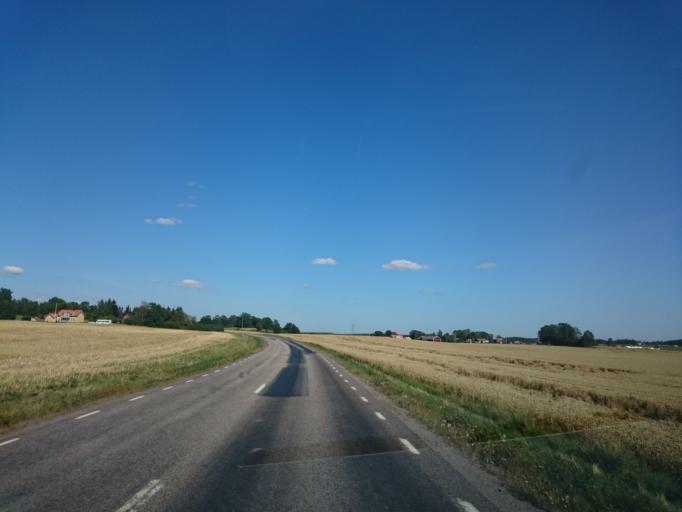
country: SE
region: OEstergoetland
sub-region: Linkopings Kommun
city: Sturefors
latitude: 58.3858
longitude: 15.7407
